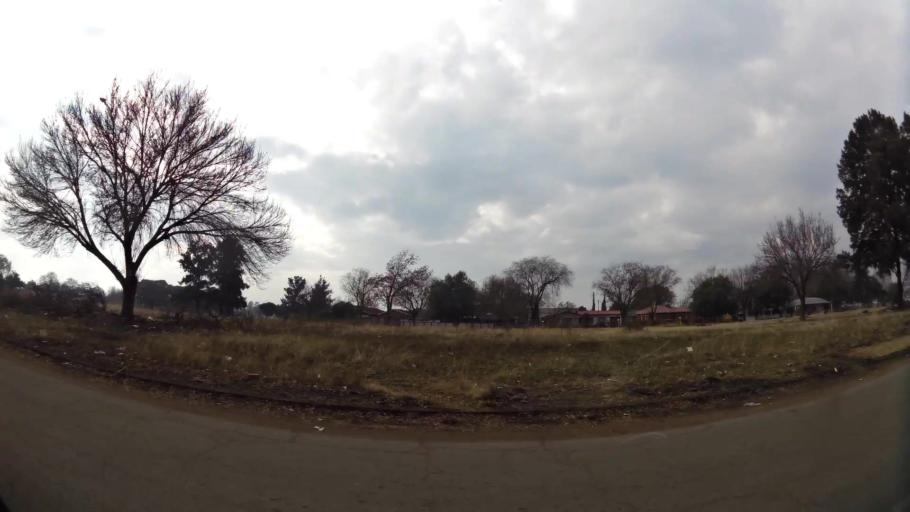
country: ZA
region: Gauteng
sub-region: Sedibeng District Municipality
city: Vanderbijlpark
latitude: -26.6821
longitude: 27.8327
